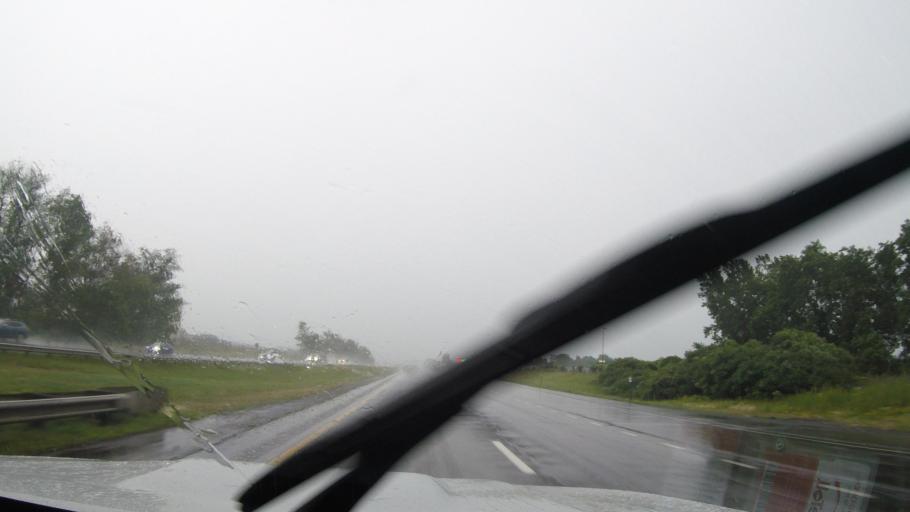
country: US
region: New York
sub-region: Seneca County
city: Waterloo
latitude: 42.9677
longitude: -76.8472
